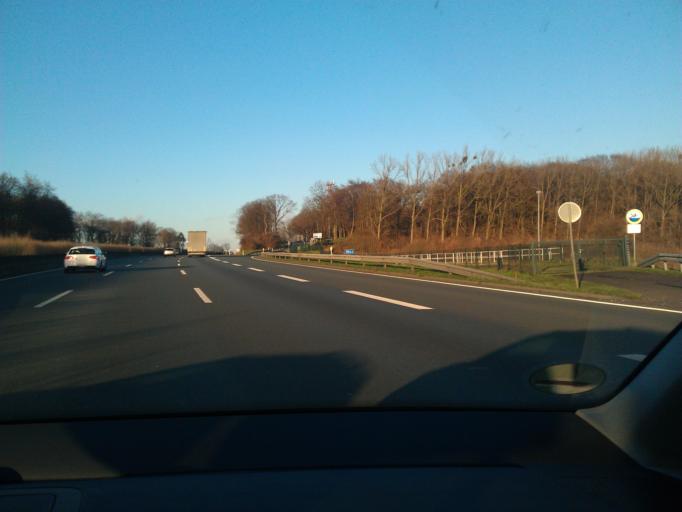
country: DE
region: North Rhine-Westphalia
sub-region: Regierungsbezirk Munster
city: Beckum
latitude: 51.7208
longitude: 7.9796
